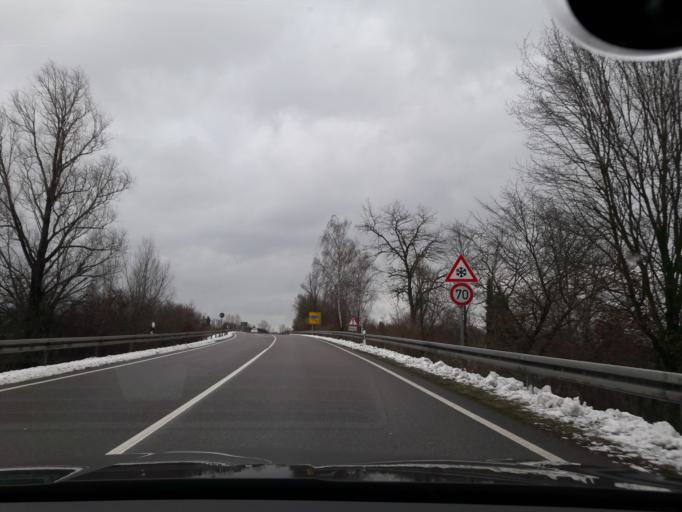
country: DE
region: Bavaria
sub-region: Upper Bavaria
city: Karlsfeld
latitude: 48.2494
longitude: 11.4745
